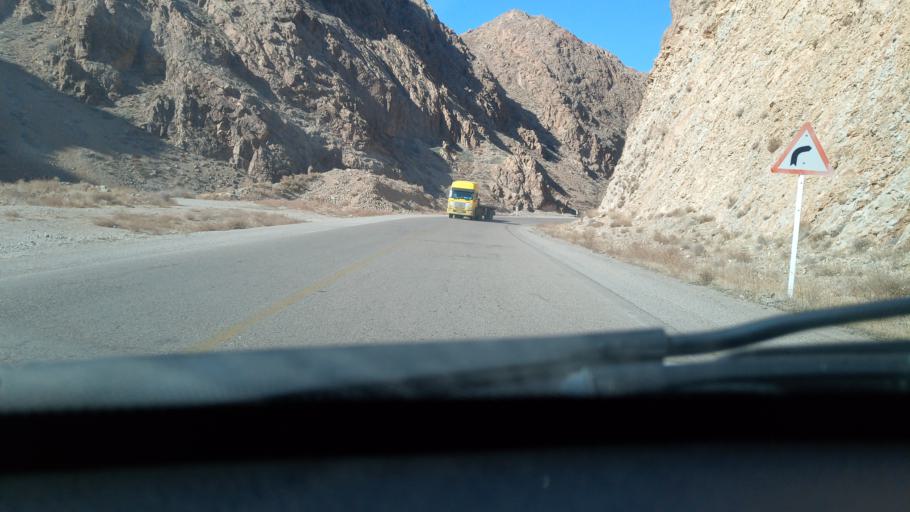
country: IR
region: Khorasan-e Shomali
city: Esfarayen
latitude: 37.1714
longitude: 57.4237
